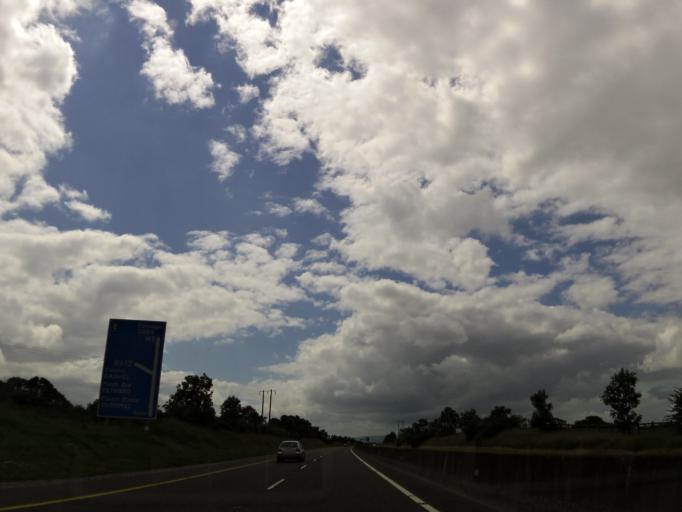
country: IE
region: Munster
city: Cashel
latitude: 52.5183
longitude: -7.8612
